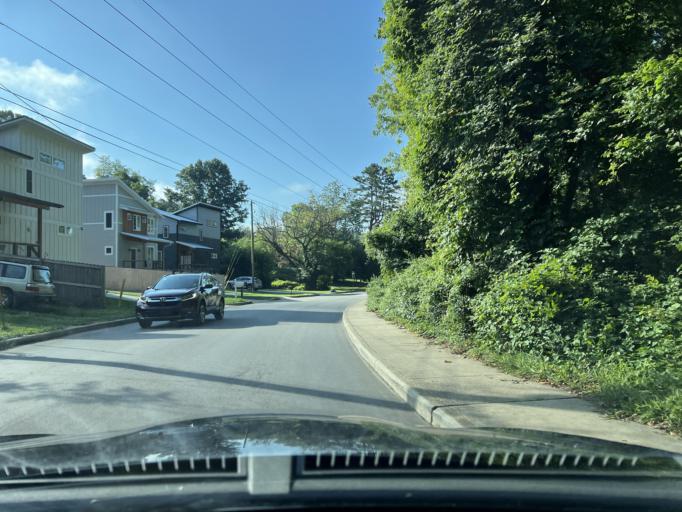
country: US
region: North Carolina
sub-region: Buncombe County
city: Asheville
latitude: 35.5686
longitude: -82.5745
